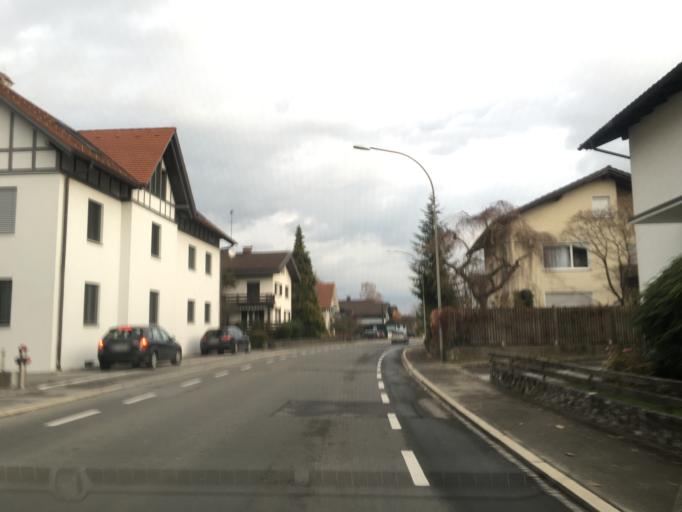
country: AT
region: Vorarlberg
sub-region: Politischer Bezirk Feldkirch
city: Gotzis
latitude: 47.3379
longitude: 9.6401
